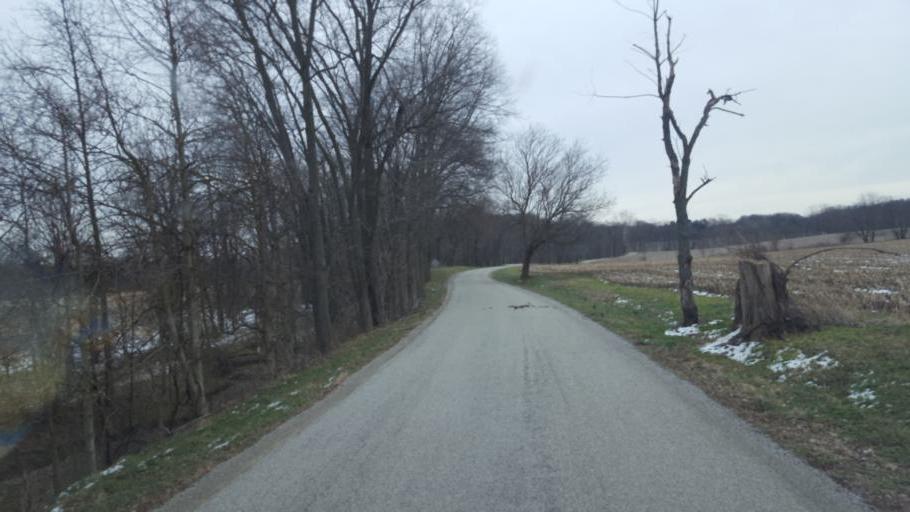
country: US
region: Ohio
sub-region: Sandusky County
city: Bellville
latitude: 40.5961
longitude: -82.4592
